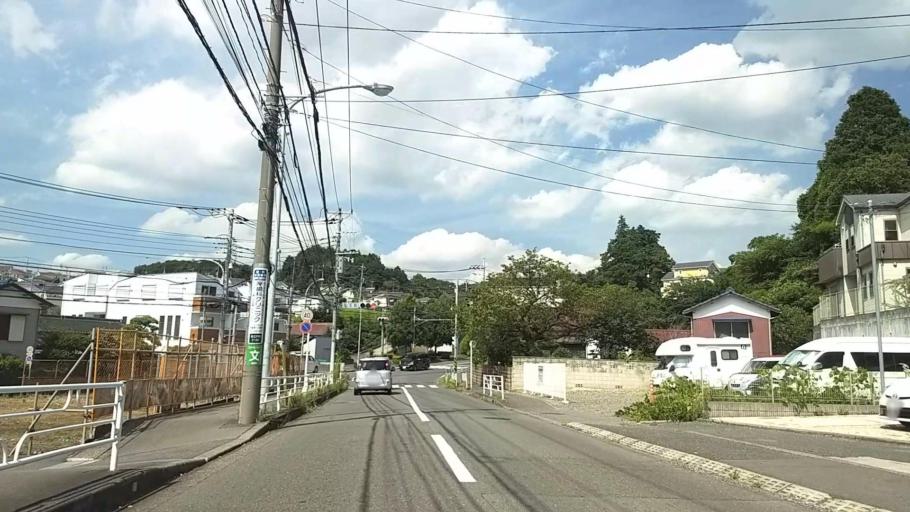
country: JP
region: Kanagawa
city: Yokohama
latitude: 35.5207
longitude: 139.5619
